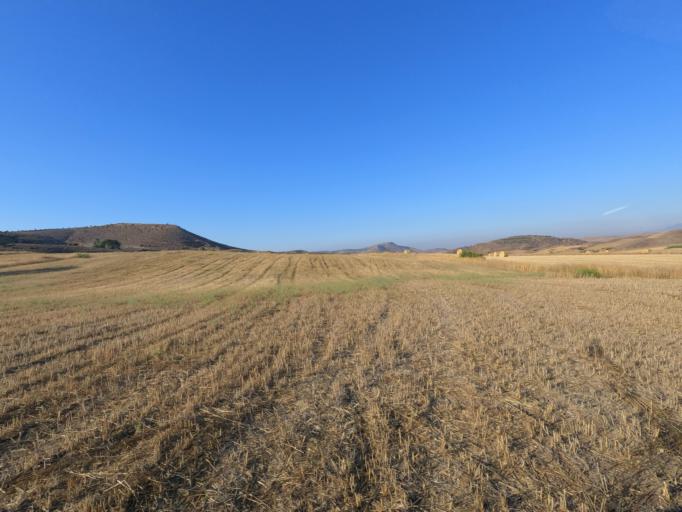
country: CY
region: Larnaka
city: Troulloi
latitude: 35.0258
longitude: 33.6496
